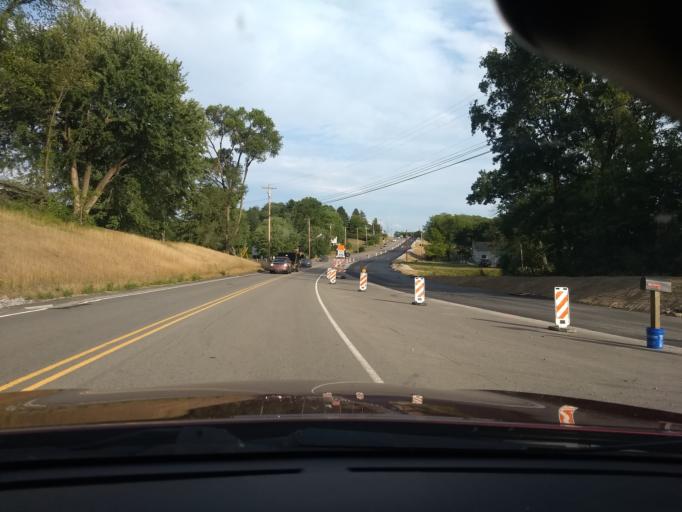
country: US
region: Pennsylvania
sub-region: Armstrong County
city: Freeport
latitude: 40.6609
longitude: -79.6744
